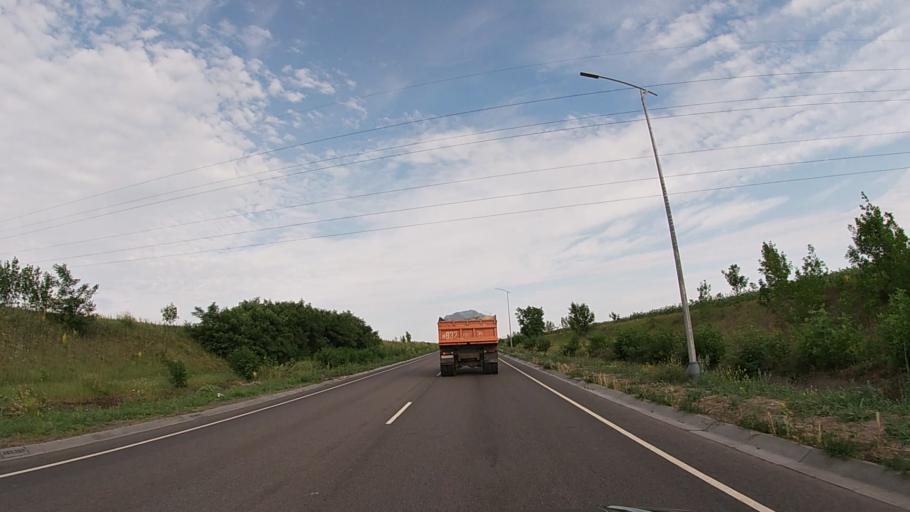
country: RU
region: Belgorod
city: Severnyy
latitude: 50.6702
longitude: 36.4854
